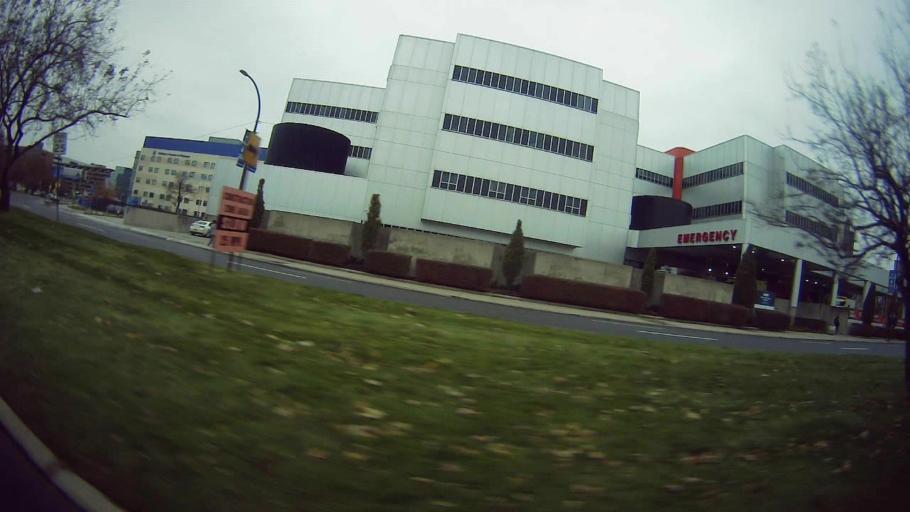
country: US
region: Michigan
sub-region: Wayne County
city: Detroit
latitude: 42.3537
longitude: -83.0530
